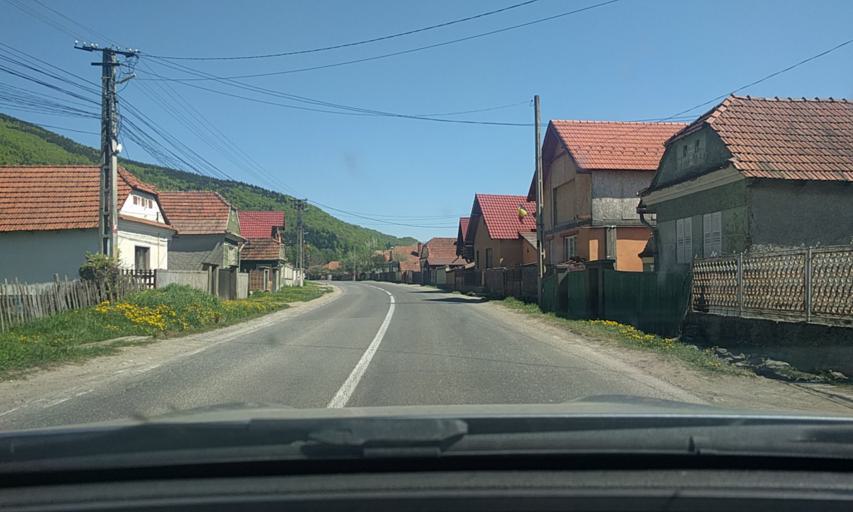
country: RO
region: Brasov
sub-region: Comuna Teliu
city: Teliu
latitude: 45.6907
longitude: 25.8806
